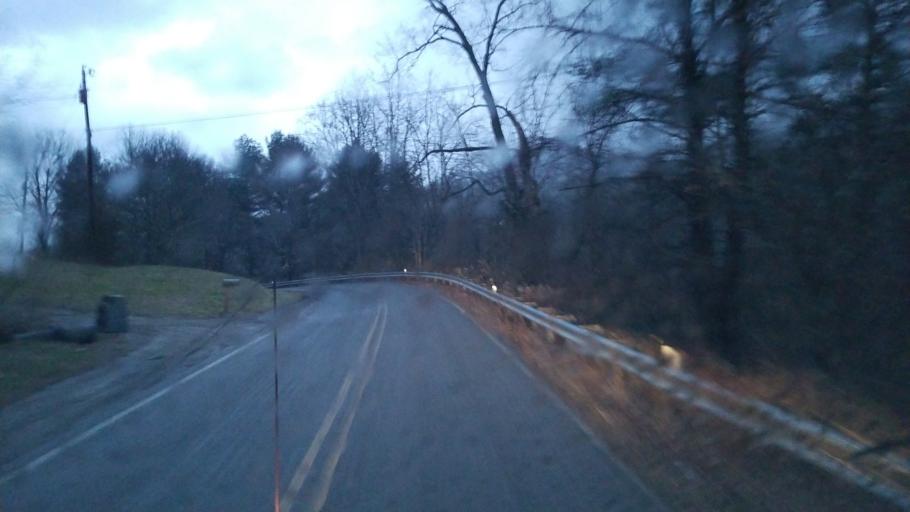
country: US
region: Virginia
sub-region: Pulaski County
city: Pulaski
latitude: 37.1242
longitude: -80.8670
